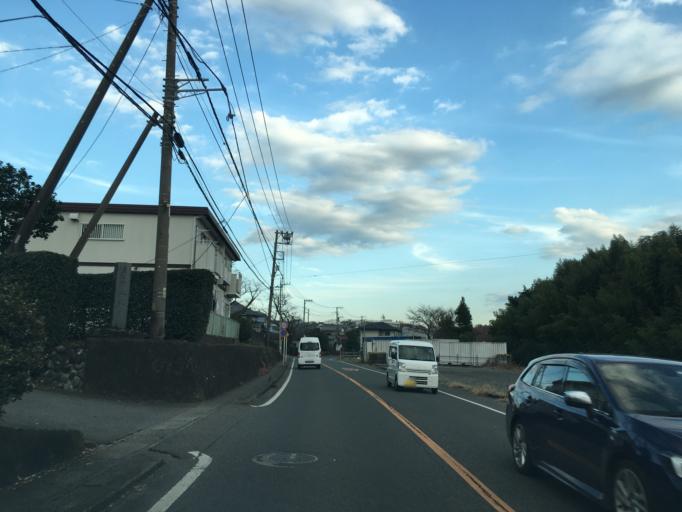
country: JP
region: Tokyo
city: Hachioji
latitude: 35.5709
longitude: 139.3428
